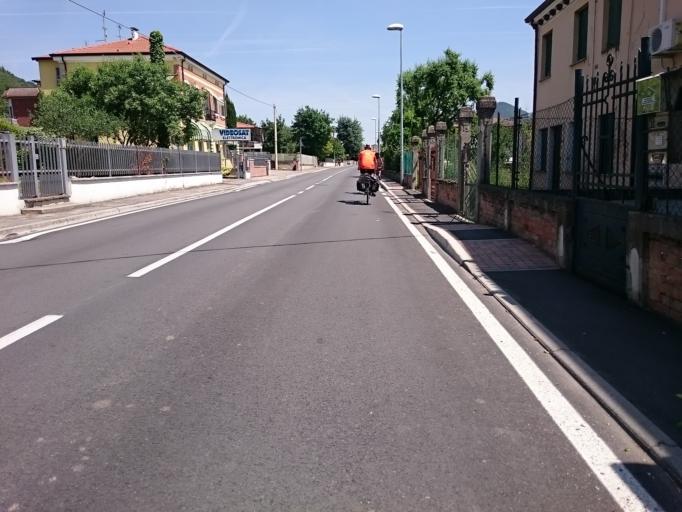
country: IT
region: Veneto
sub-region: Provincia di Padova
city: Lozzo Atestino
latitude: 45.2883
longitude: 11.6273
